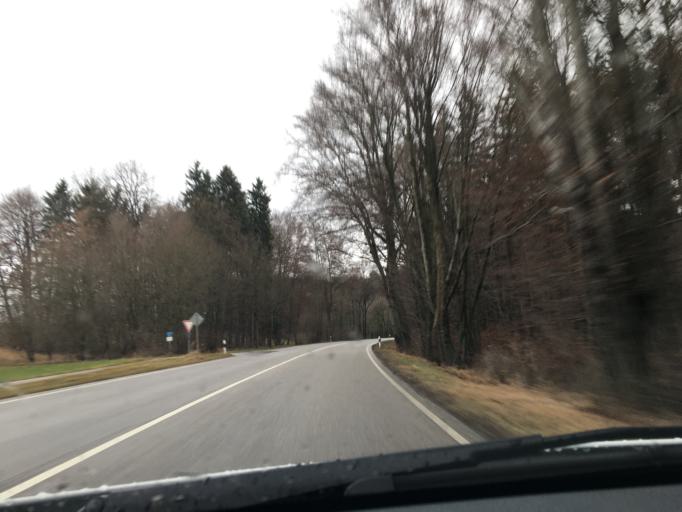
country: DE
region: Bavaria
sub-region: Upper Bavaria
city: Icking
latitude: 47.9383
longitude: 11.4227
